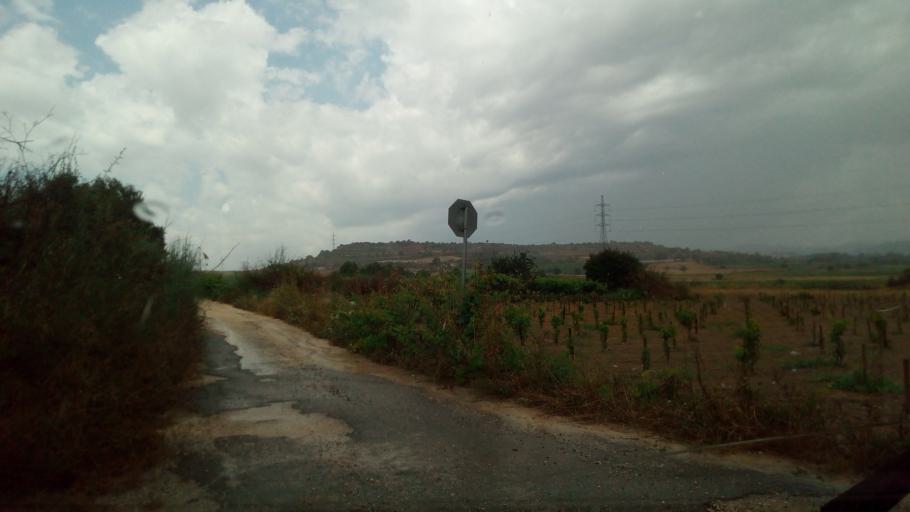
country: CY
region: Pafos
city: Tala
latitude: 34.8876
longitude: 32.4902
